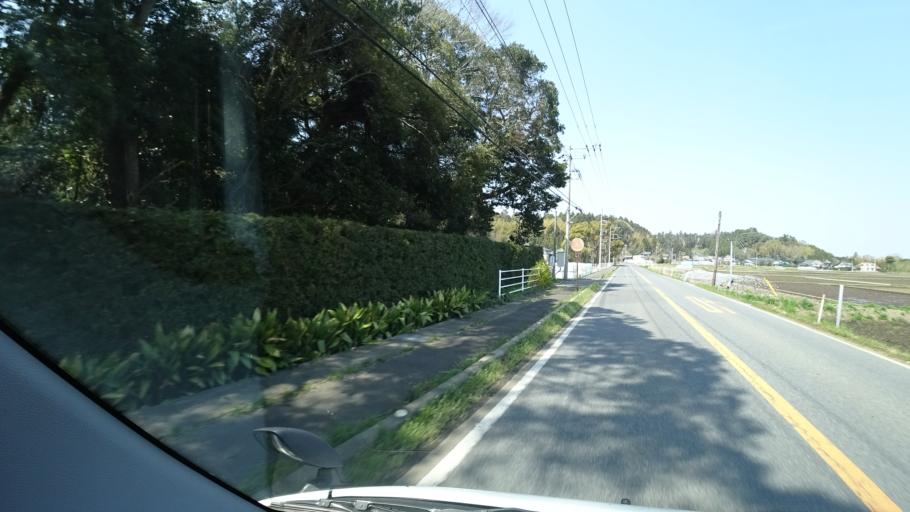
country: JP
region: Chiba
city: Yokaichiba
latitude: 35.6806
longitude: 140.4644
